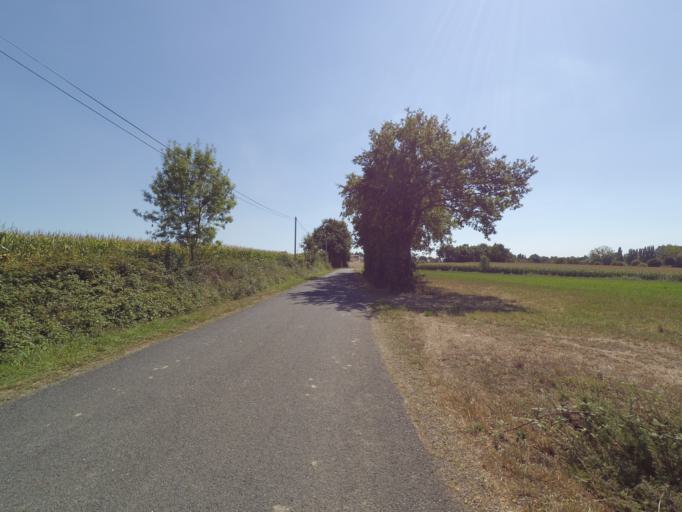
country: FR
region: Pays de la Loire
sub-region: Departement de la Loire-Atlantique
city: Vieillevigne
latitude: 46.9765
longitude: -1.4253
